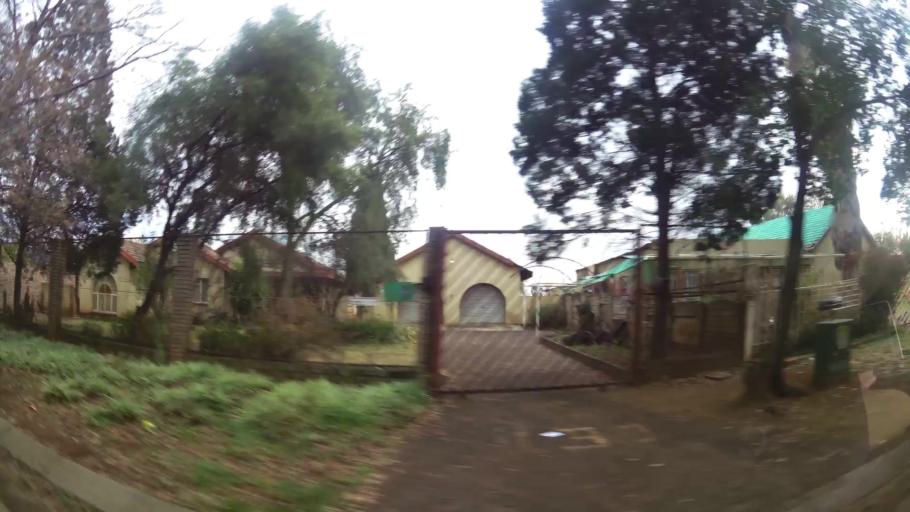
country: ZA
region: Gauteng
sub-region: Sedibeng District Municipality
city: Meyerton
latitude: -26.5905
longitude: 27.9937
